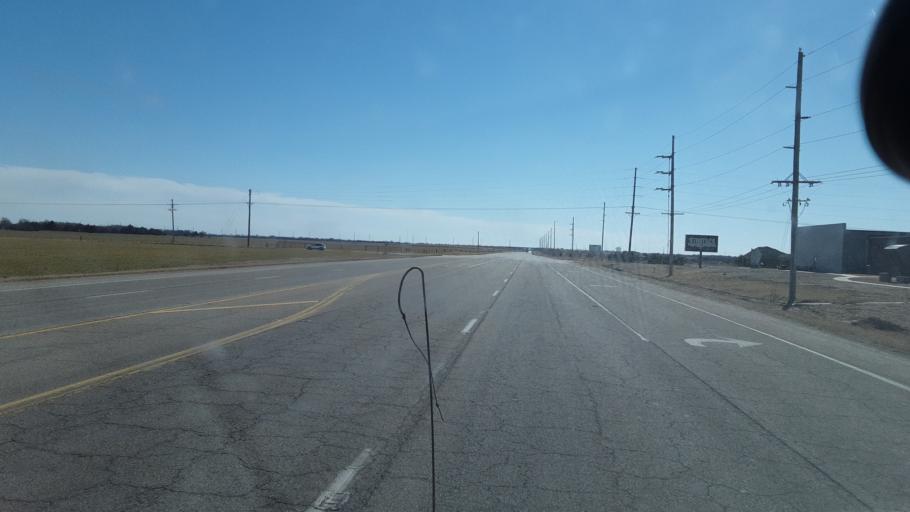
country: US
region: Kansas
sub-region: Reno County
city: Hutchinson
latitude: 38.0448
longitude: -97.8670
